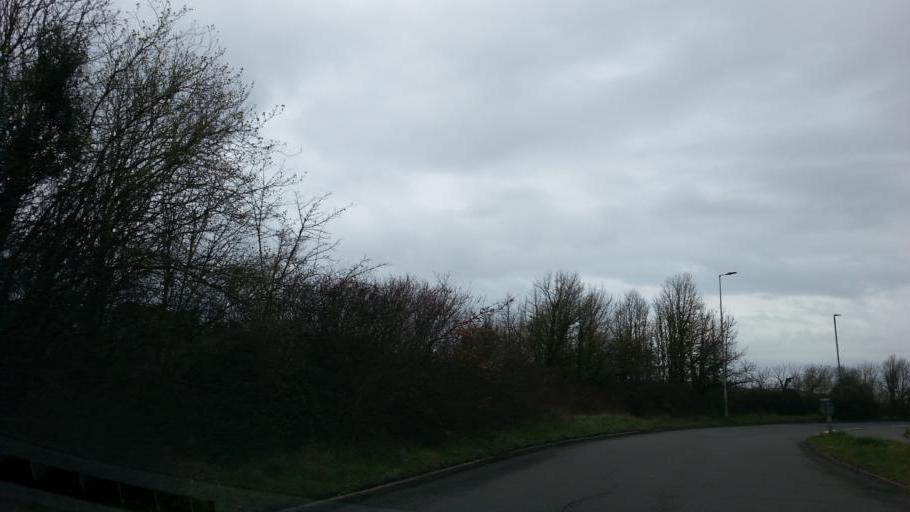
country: GB
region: England
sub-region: Devon
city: Appledore
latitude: 51.0326
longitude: -4.1961
